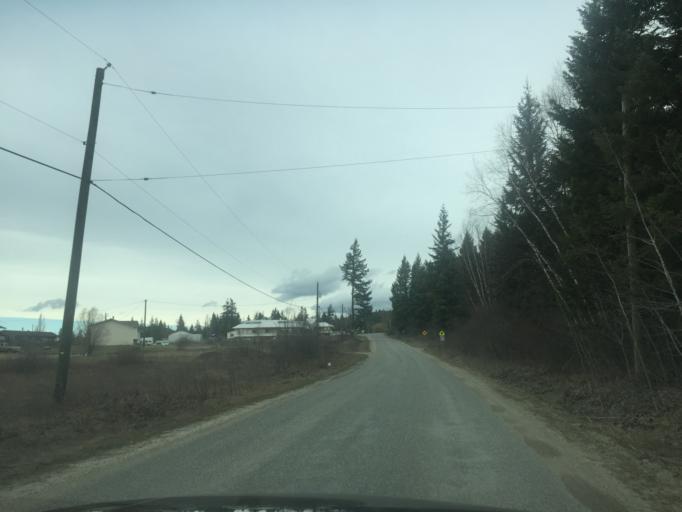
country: CA
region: British Columbia
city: Kamloops
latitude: 51.3147
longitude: -120.1496
